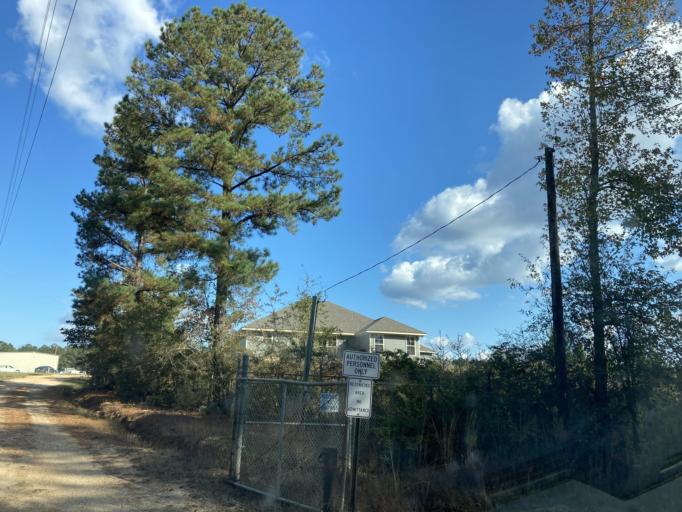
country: US
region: Mississippi
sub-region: Lamar County
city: Sumrall
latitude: 31.4302
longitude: -89.5359
